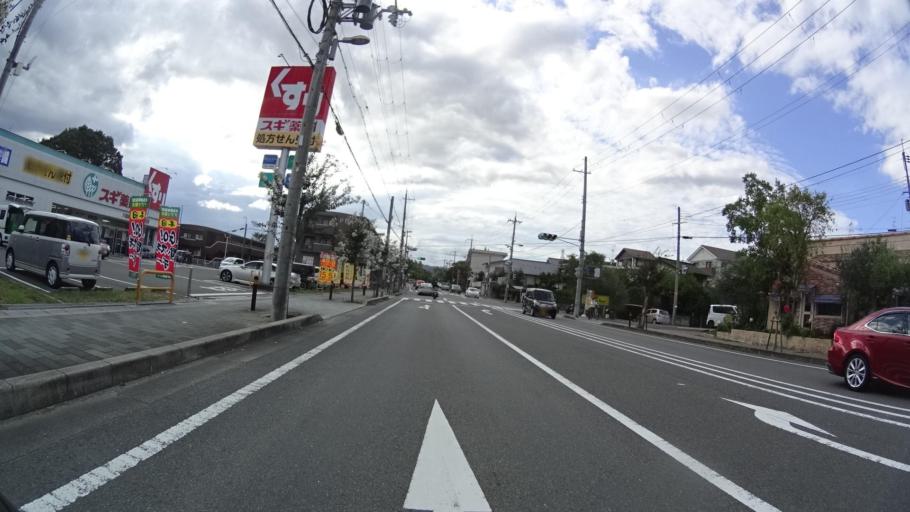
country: JP
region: Kyoto
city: Yawata
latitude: 34.8552
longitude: 135.6995
